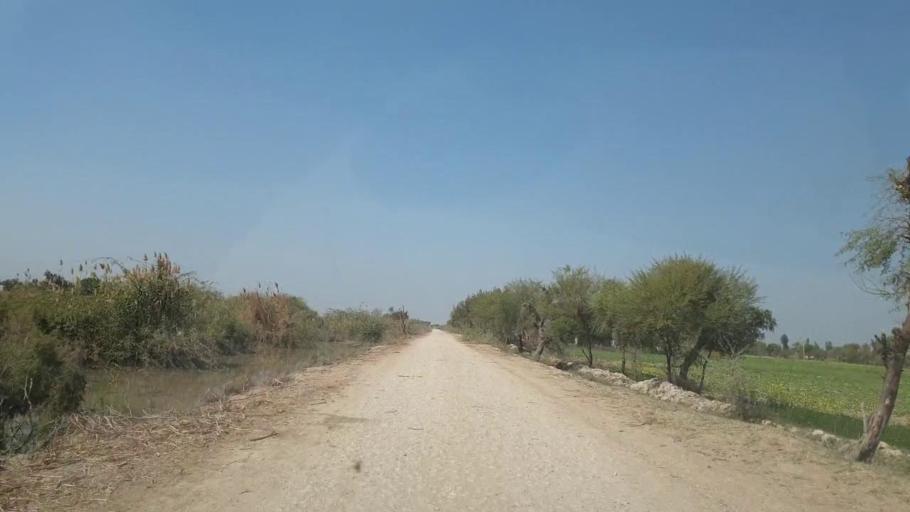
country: PK
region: Sindh
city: Mirpur Khas
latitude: 25.7302
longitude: 69.0671
